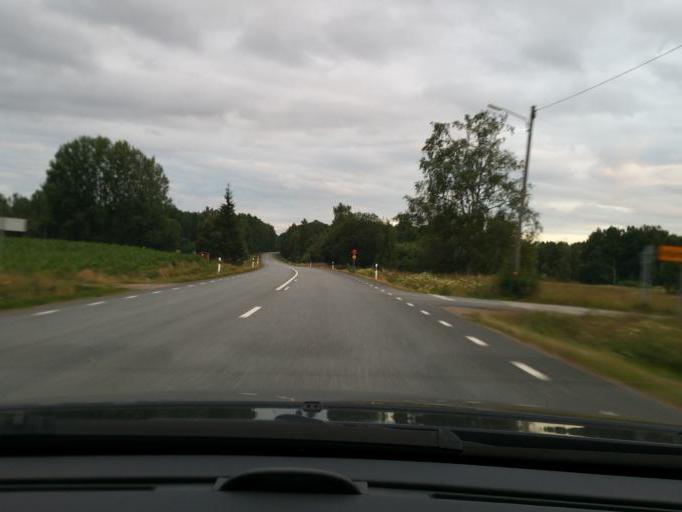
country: SE
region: Kronoberg
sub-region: Alvesta Kommun
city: Alvesta
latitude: 56.9333
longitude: 14.5587
